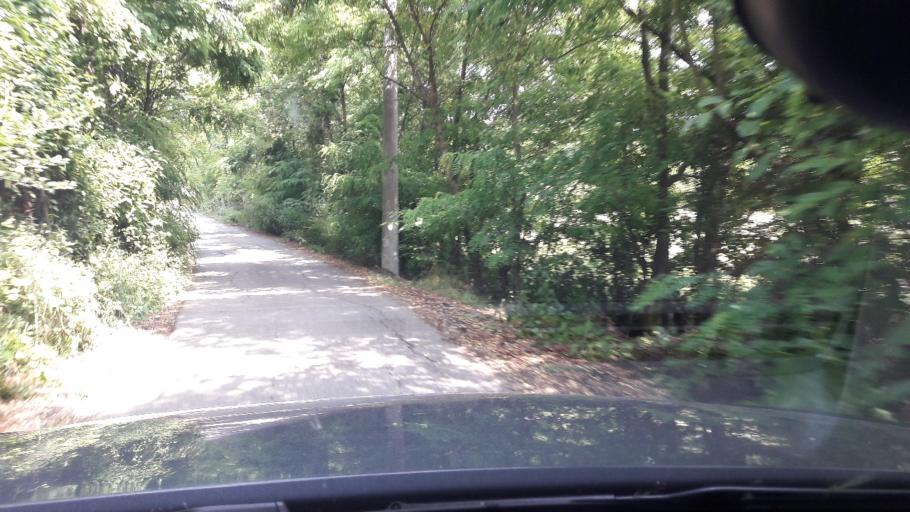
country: RS
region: Central Serbia
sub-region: Belgrade
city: Sopot
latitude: 44.6140
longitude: 20.5906
